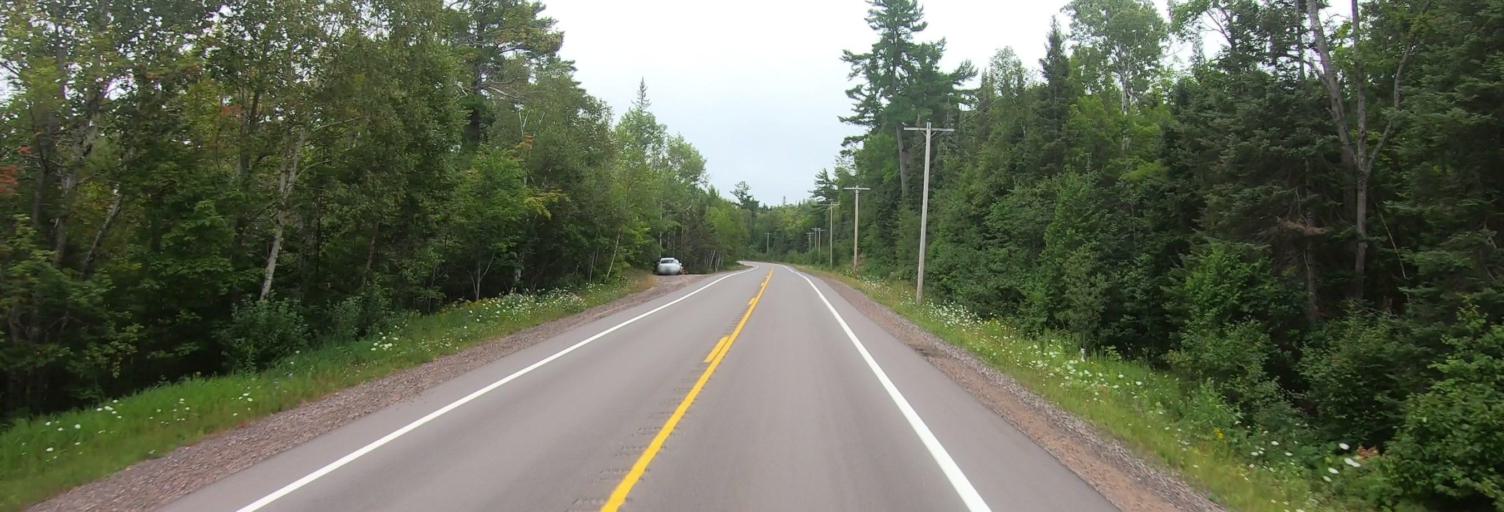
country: US
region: Michigan
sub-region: Keweenaw County
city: Eagle River
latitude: 47.3978
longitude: -88.2856
